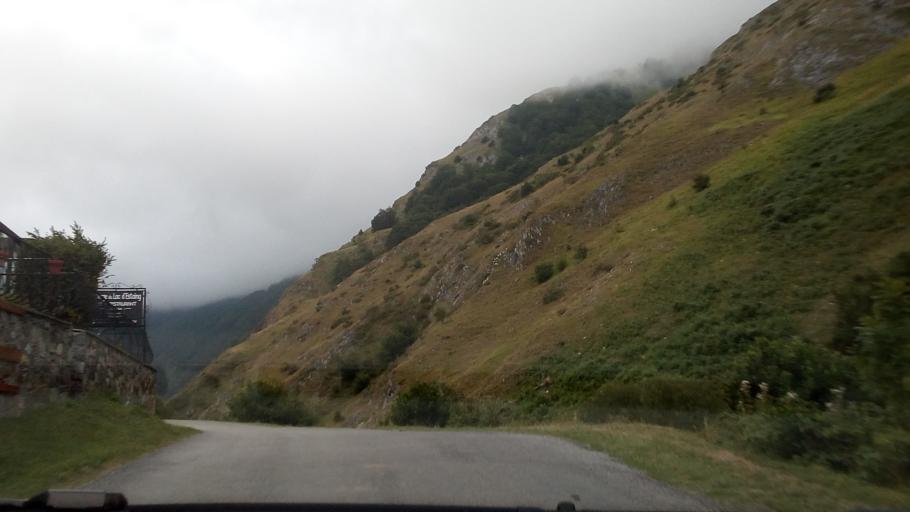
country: FR
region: Midi-Pyrenees
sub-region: Departement des Hautes-Pyrenees
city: Cauterets
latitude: 42.9104
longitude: -0.2012
